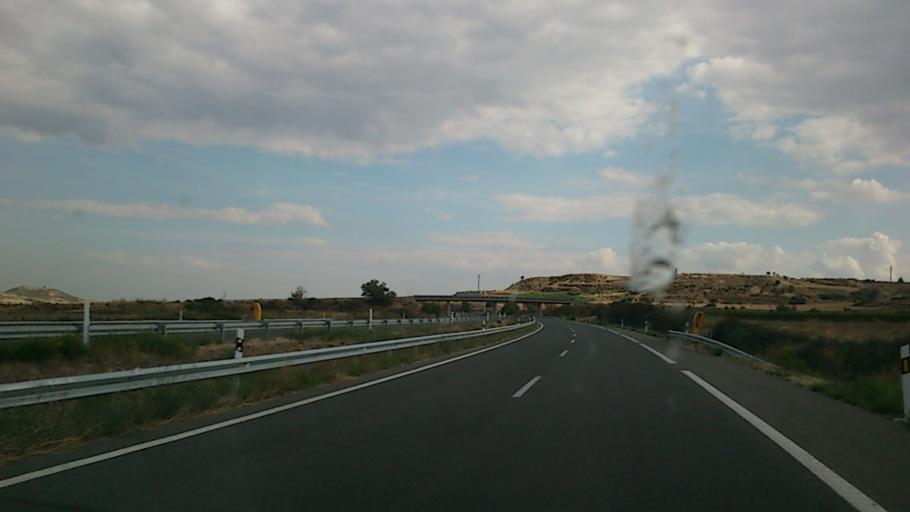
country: ES
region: La Rioja
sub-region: Provincia de La Rioja
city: Haro
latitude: 42.5546
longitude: -2.8668
